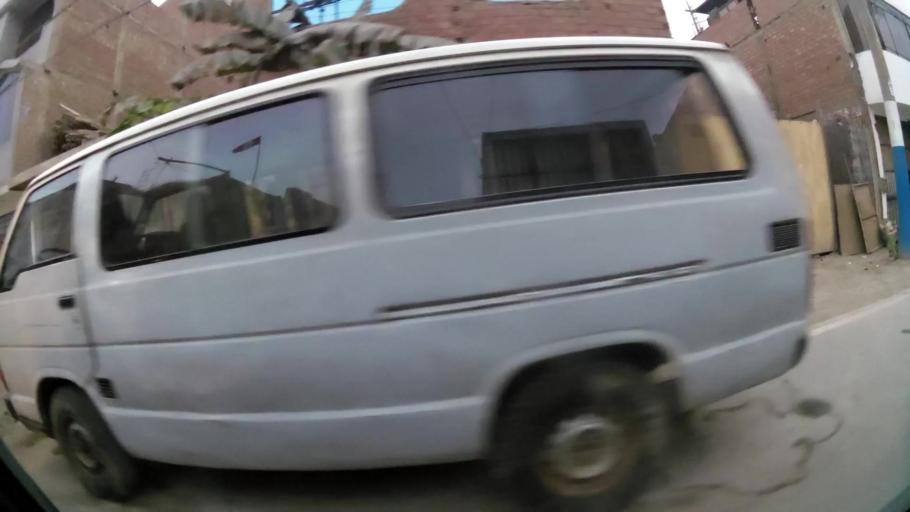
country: PE
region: Lima
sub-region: Lima
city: Independencia
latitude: -11.9778
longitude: -77.0945
